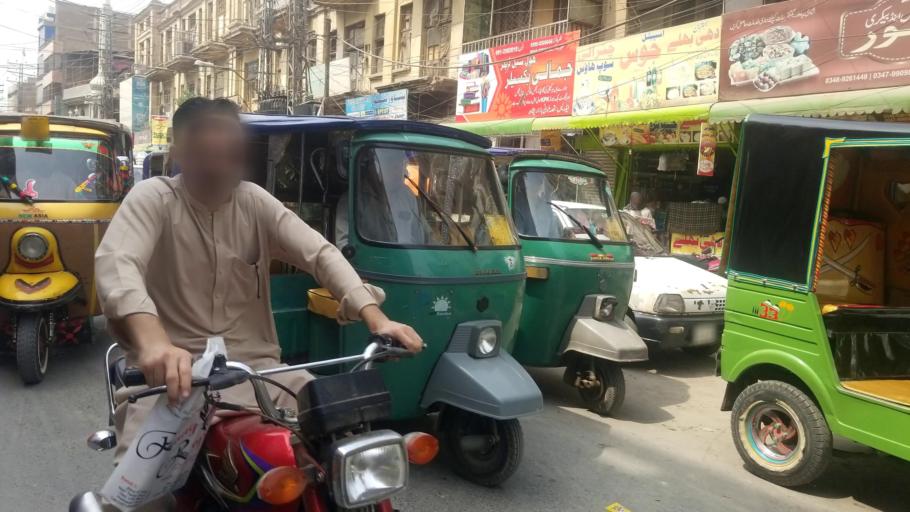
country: PK
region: Khyber Pakhtunkhwa
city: Peshawar
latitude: 34.0079
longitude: 71.5700
